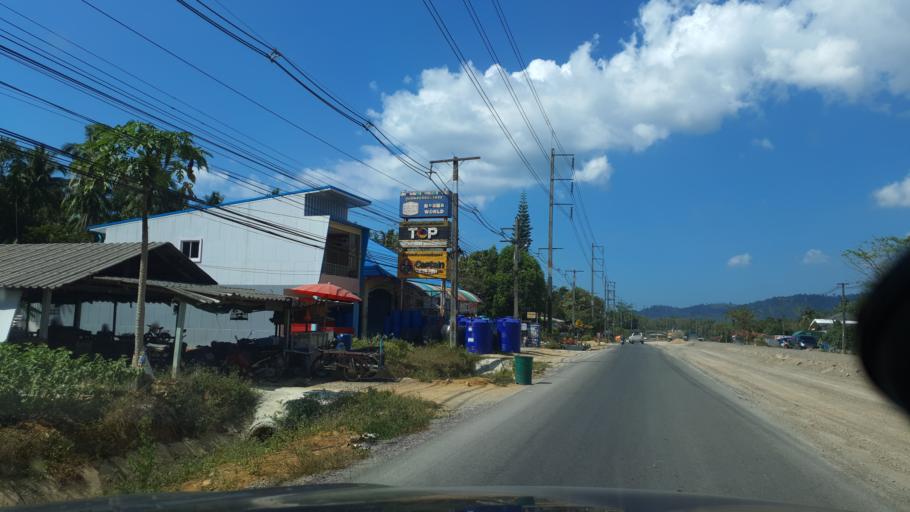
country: TH
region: Phangnga
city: Ban Khao Lak
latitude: 8.5690
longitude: 98.2652
